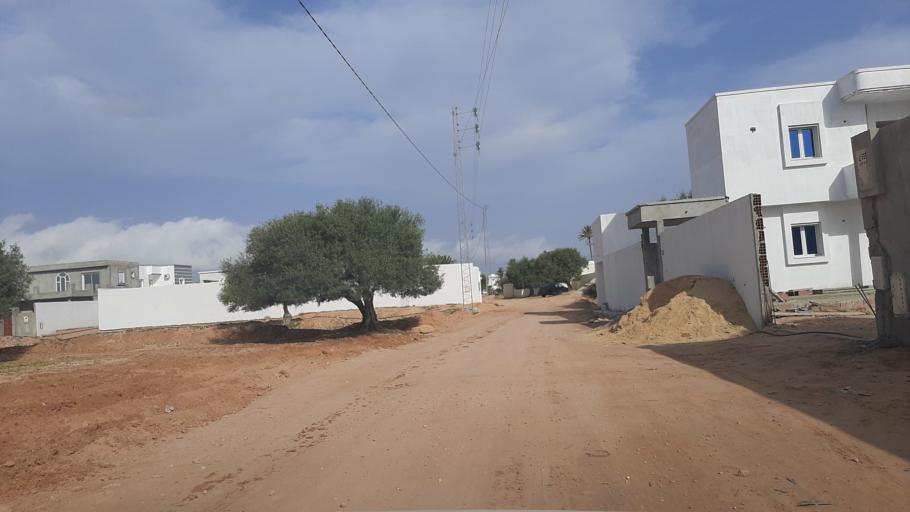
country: TN
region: Madanin
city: Midoun
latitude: 33.8011
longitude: 11.0265
